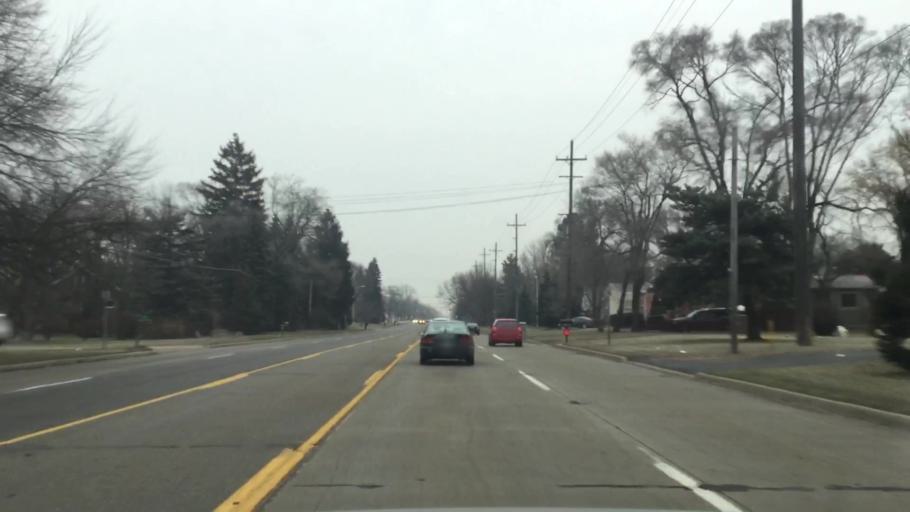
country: US
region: Michigan
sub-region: Oakland County
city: Farmington
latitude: 42.4222
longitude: -83.3551
